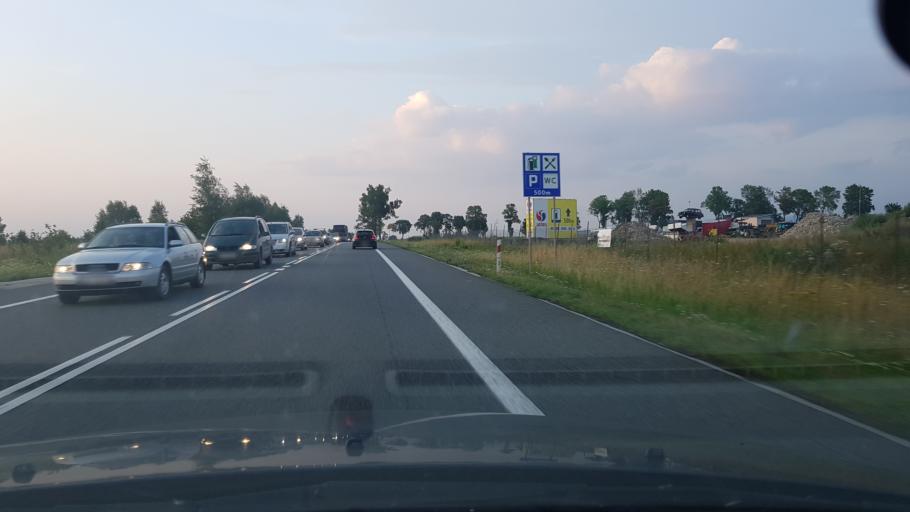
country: PL
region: Masovian Voivodeship
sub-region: Powiat mlawski
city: Wieczfnia Koscielna
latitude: 53.1940
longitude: 20.4348
